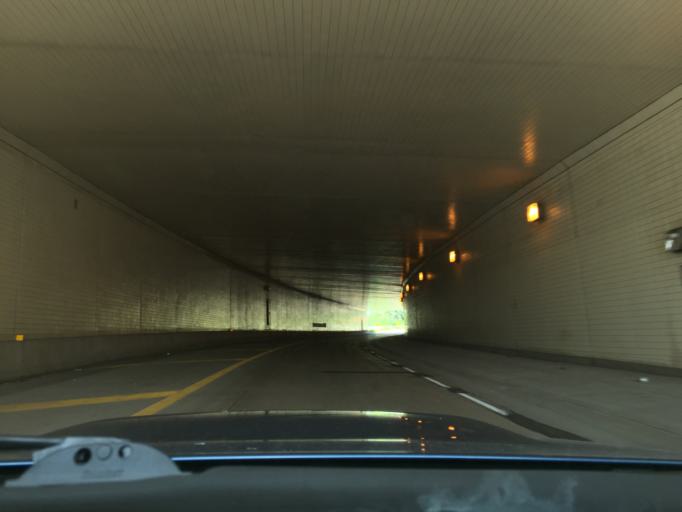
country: US
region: Minnesota
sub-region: Ramsey County
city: Saint Paul
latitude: 44.9488
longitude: -93.1058
